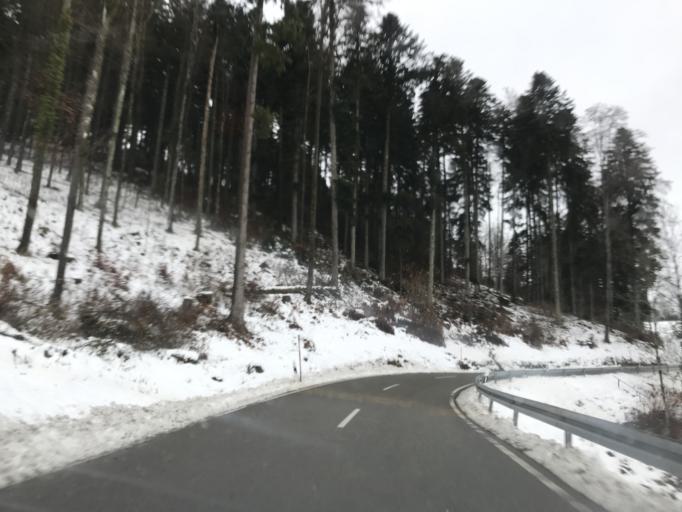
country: DE
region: Baden-Wuerttemberg
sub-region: Freiburg Region
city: Hasel
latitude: 47.6911
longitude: 7.8927
